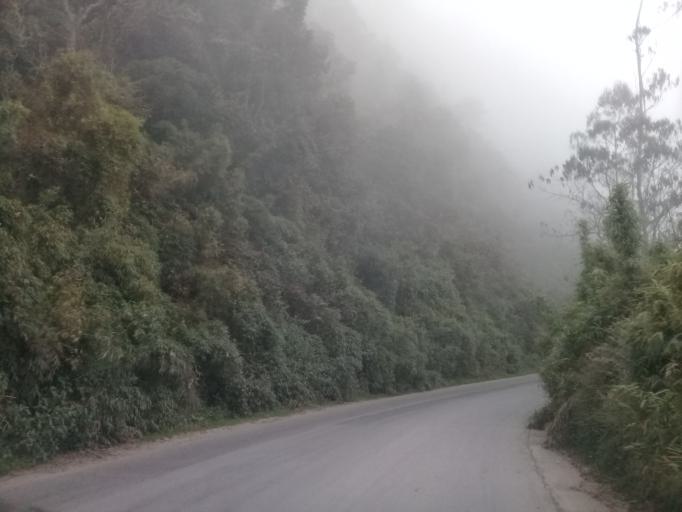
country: CO
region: Cundinamarca
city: Zipaquira
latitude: 5.0880
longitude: -74.0688
